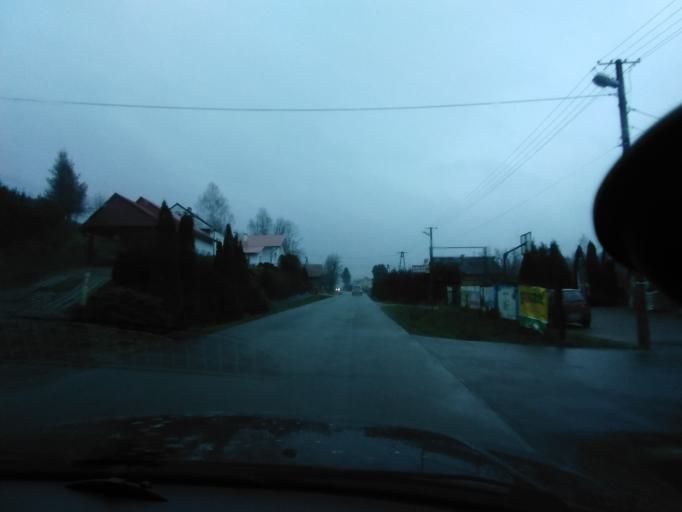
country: PL
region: Subcarpathian Voivodeship
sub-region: Powiat brzozowski
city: Wesola
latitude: 49.7493
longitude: 22.1203
